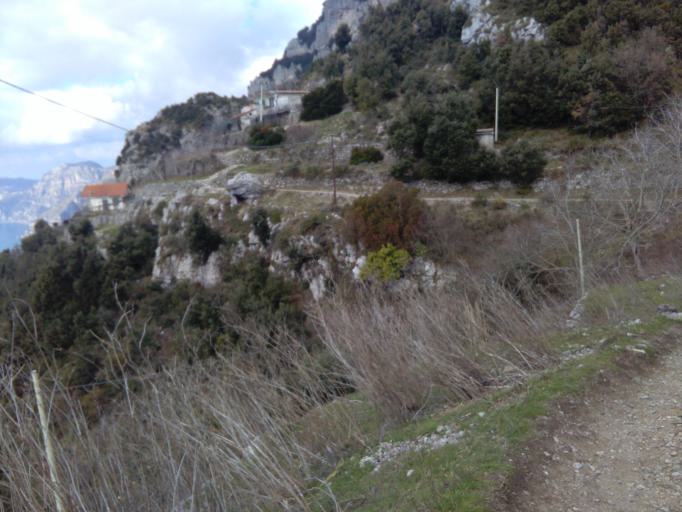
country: IT
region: Campania
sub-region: Provincia di Salerno
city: Praiano
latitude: 40.6209
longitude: 14.5278
